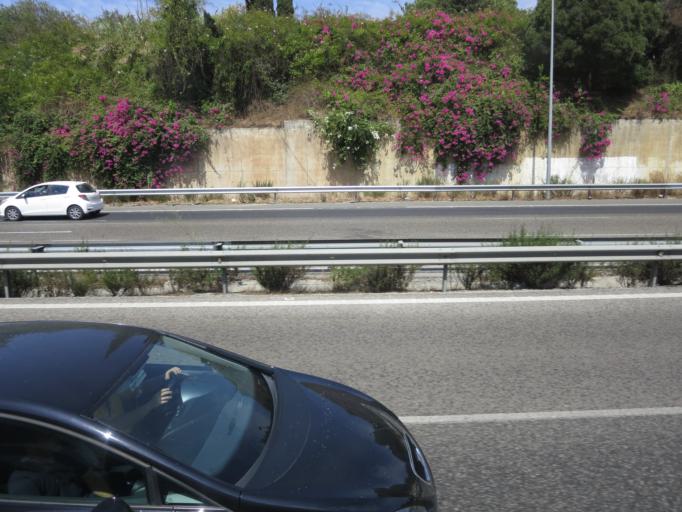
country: ES
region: Andalusia
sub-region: Provincia de Malaga
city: Marbella
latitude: 36.5158
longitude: -4.9087
